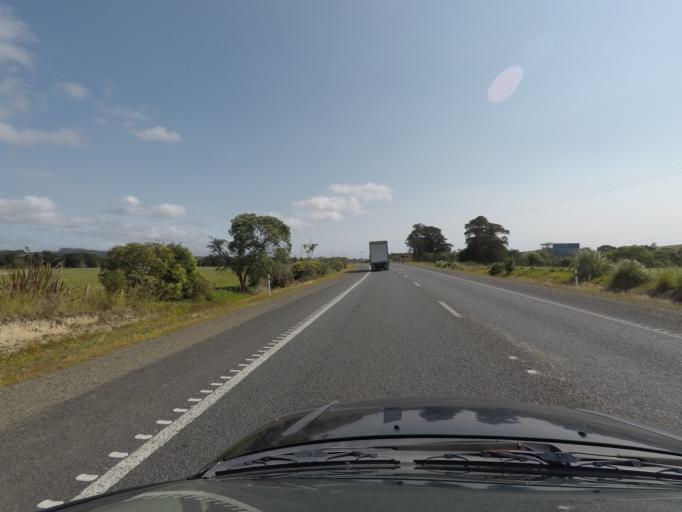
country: NZ
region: Northland
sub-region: Whangarei
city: Ruakaka
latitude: -36.0266
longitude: 174.4169
